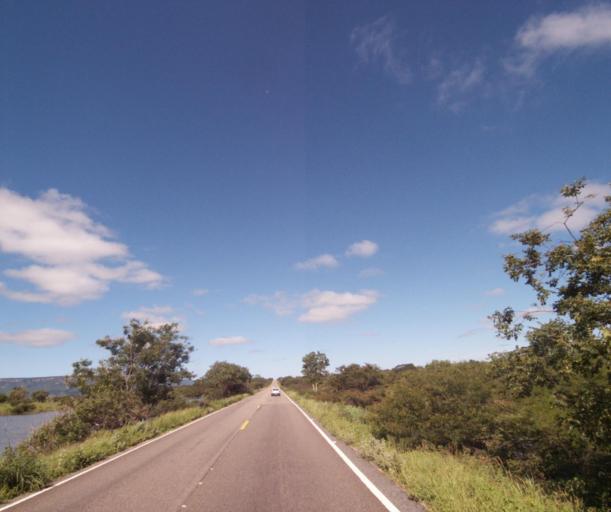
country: BR
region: Bahia
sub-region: Palmas De Monte Alto
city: Palmas de Monte Alto
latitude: -14.2396
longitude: -43.0384
